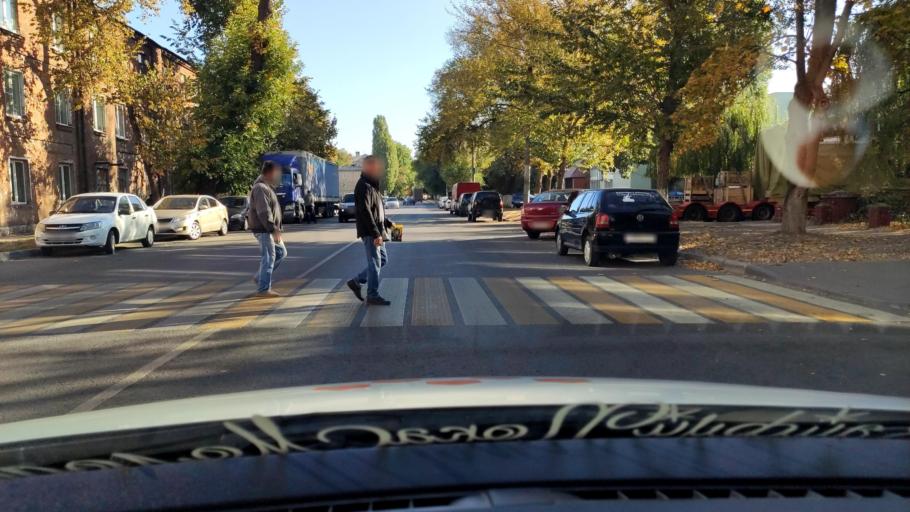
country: RU
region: Voronezj
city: Voronezh
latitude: 51.6818
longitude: 39.1980
